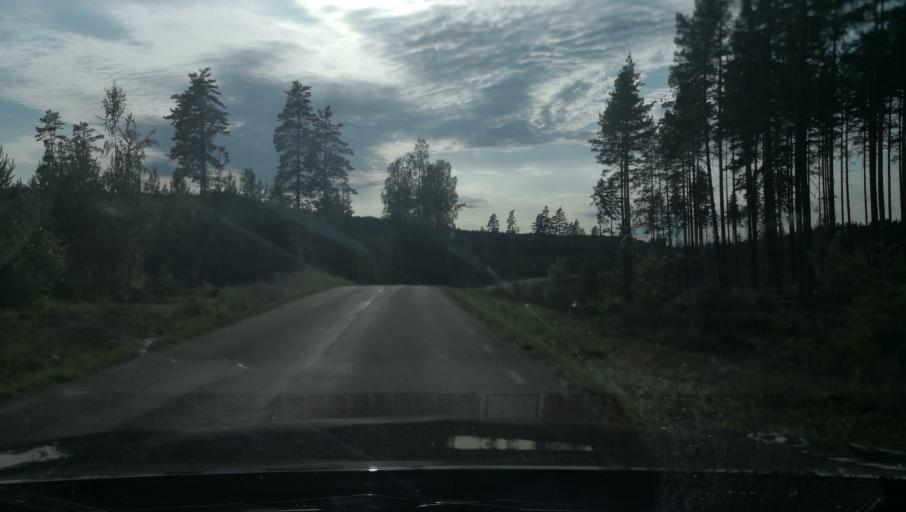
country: SE
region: Dalarna
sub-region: Smedjebackens Kommun
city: Smedjebacken
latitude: 60.0413
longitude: 15.2978
